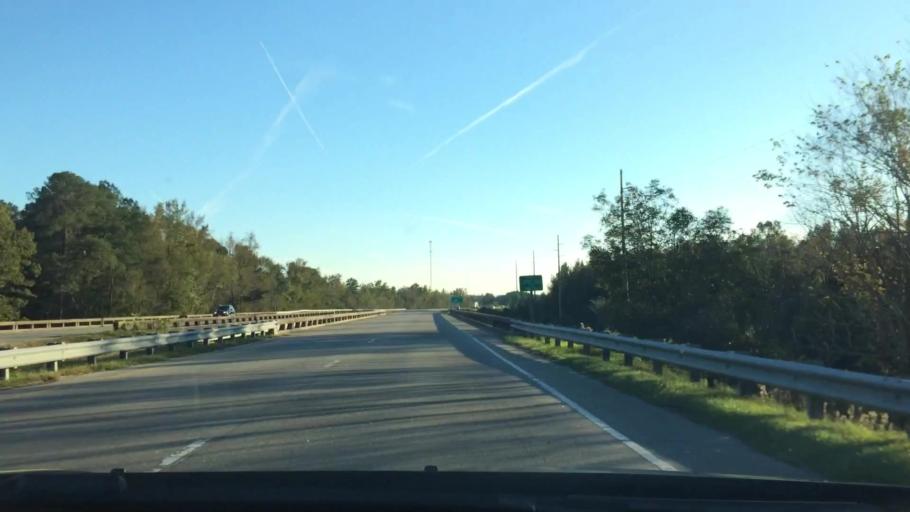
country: US
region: North Carolina
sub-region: Pitt County
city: Grifton
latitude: 35.3819
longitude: -77.4497
